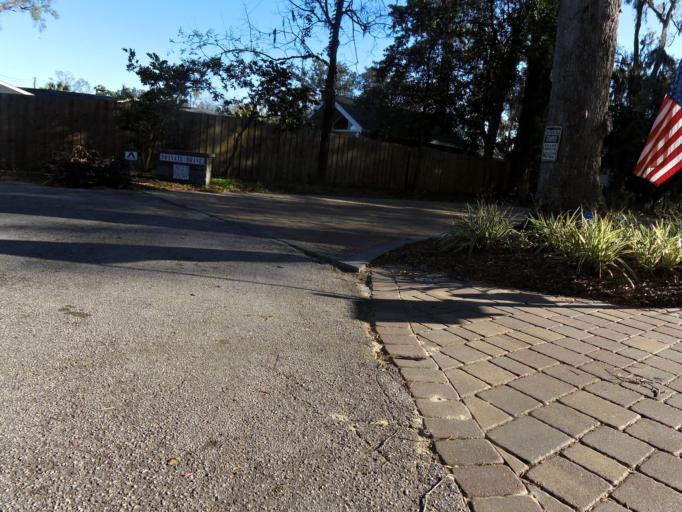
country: US
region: Florida
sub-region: Duval County
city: Jacksonville
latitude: 30.2740
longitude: -81.6541
